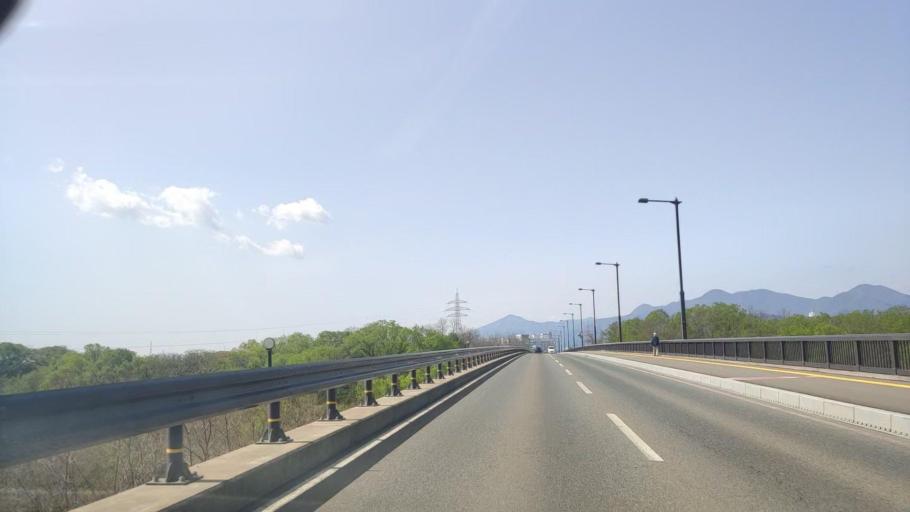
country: JP
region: Iwate
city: Morioka-shi
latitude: 39.6988
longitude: 141.1310
